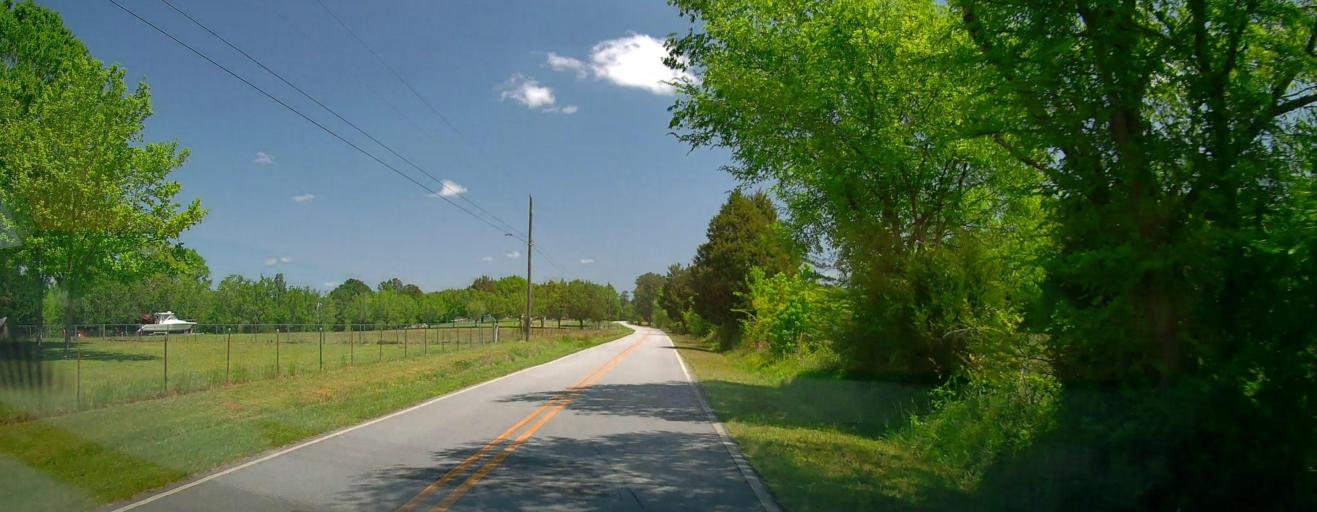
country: US
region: Georgia
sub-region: Bibb County
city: Macon
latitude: 32.9173
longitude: -83.6043
